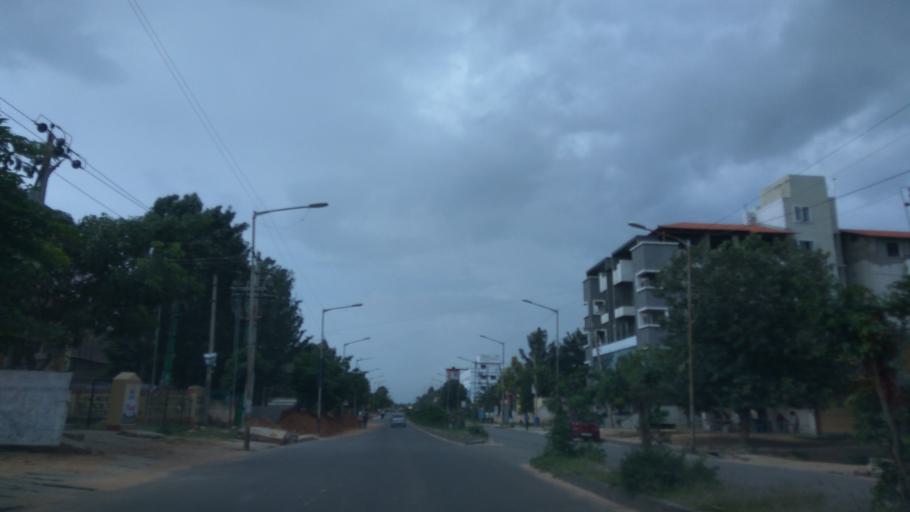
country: IN
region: Karnataka
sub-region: Bangalore Urban
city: Yelahanka
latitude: 13.0814
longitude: 77.6342
